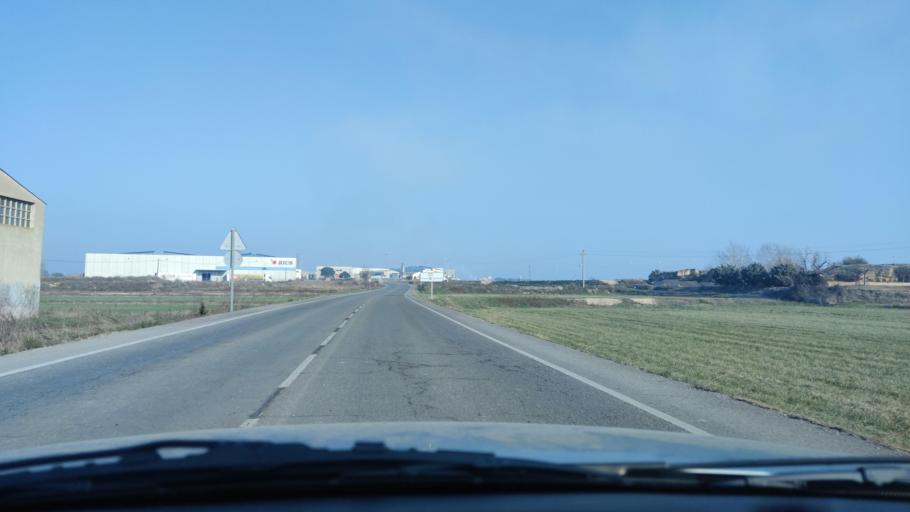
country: ES
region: Catalonia
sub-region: Provincia de Lleida
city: Torrefarrera
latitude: 41.6738
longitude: 0.6294
